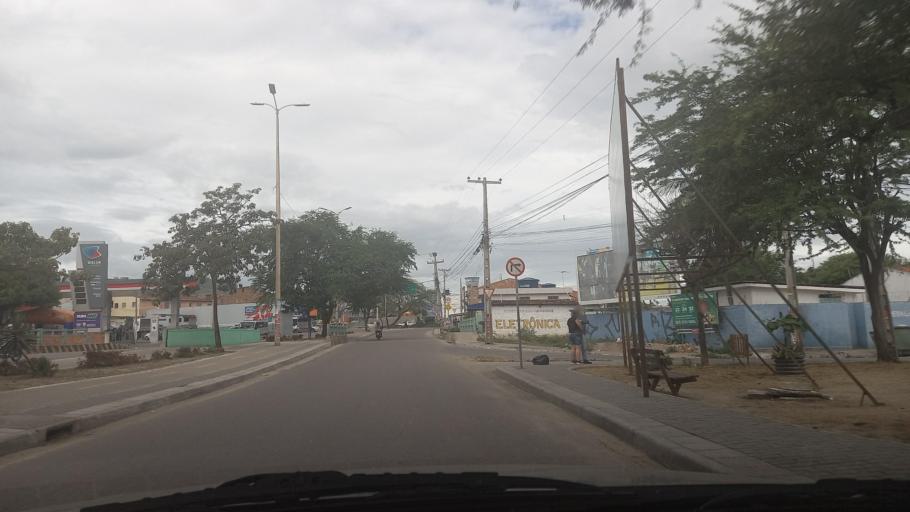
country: BR
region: Pernambuco
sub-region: Caruaru
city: Caruaru
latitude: -8.2753
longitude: -35.9857
